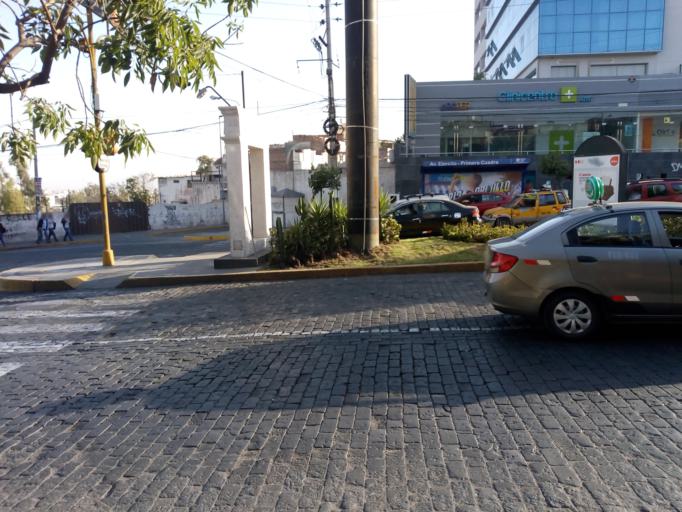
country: PE
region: Arequipa
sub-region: Provincia de Arequipa
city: Arequipa
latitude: -16.3921
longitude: -71.5407
